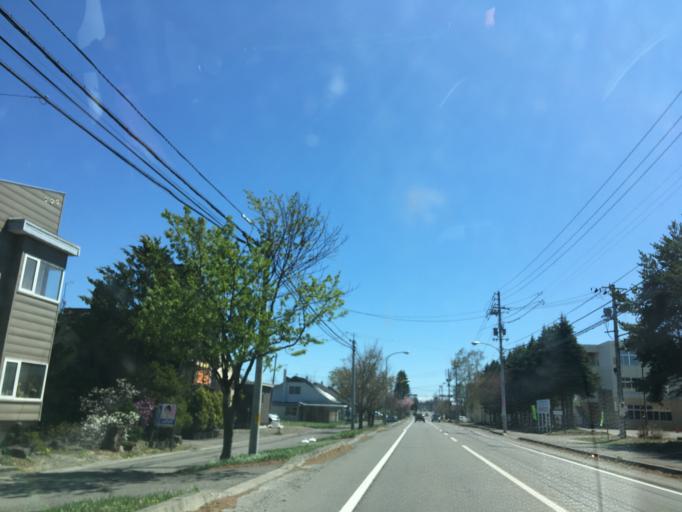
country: JP
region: Hokkaido
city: Obihiro
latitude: 42.9229
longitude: 143.1712
